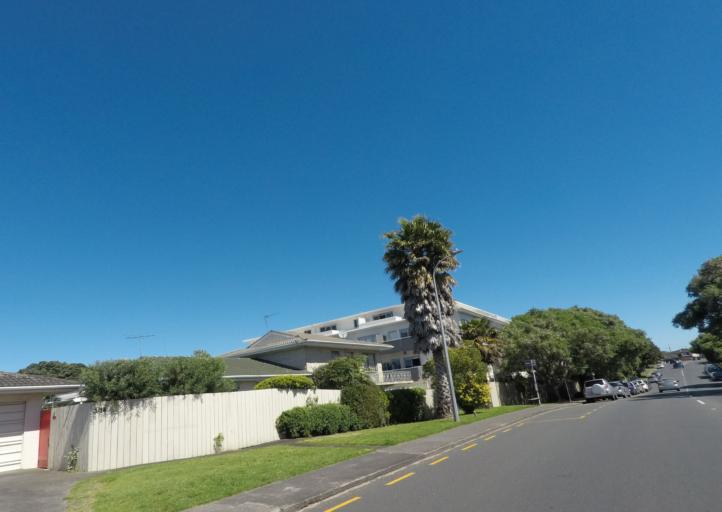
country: NZ
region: Auckland
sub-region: Auckland
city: Auckland
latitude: -36.8781
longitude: 174.7352
